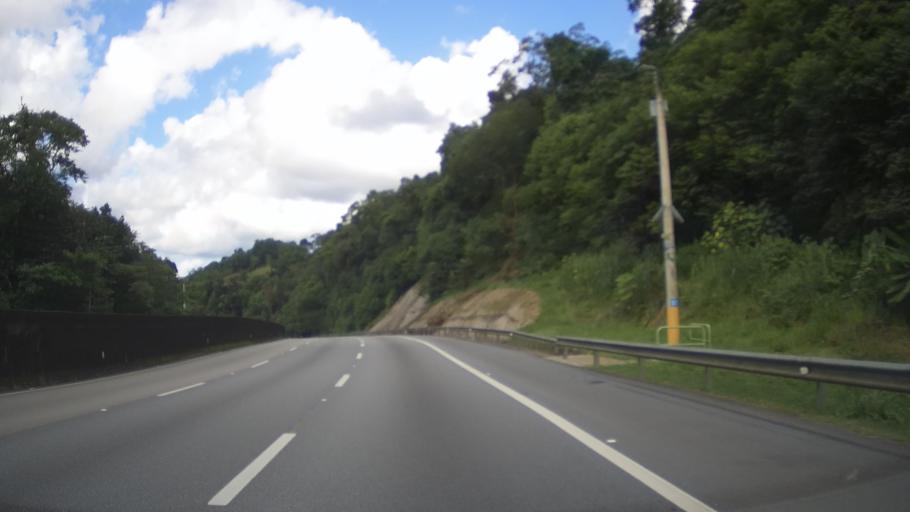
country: BR
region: Sao Paulo
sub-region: Cubatao
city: Cubatao
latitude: -23.9310
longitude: -46.4634
